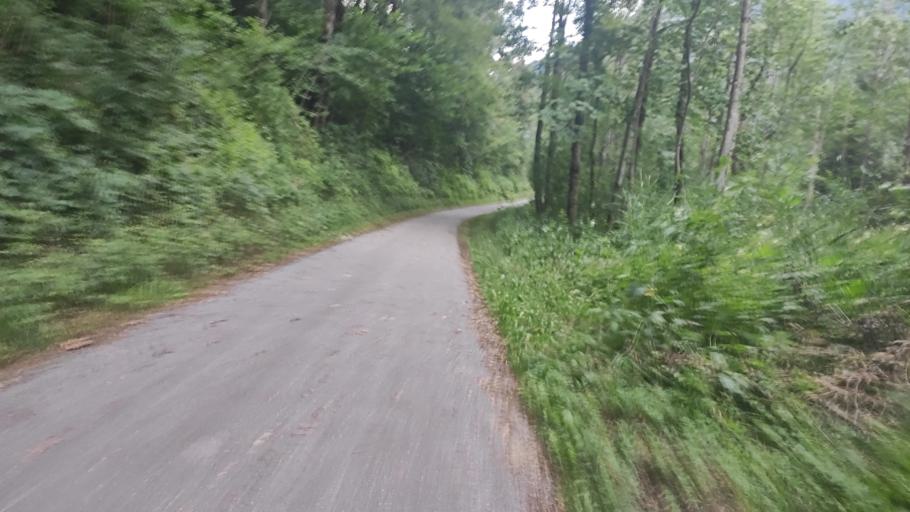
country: AT
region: Salzburg
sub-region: Politischer Bezirk Zell am See
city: Leogang
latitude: 47.5074
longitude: 12.7660
